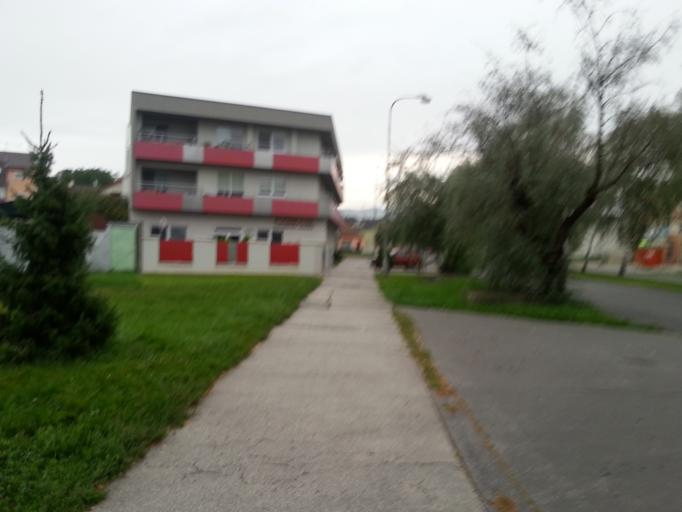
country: SK
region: Trnavsky
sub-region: Okres Trnava
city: Piestany
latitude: 48.5954
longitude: 17.8265
